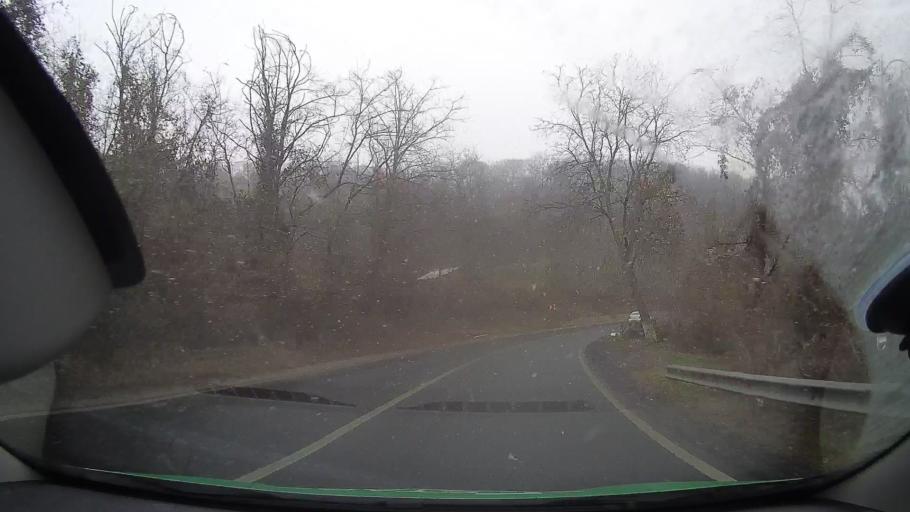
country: RO
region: Sibiu
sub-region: Municipiul Medias
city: Medias
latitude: 46.1813
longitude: 24.3368
